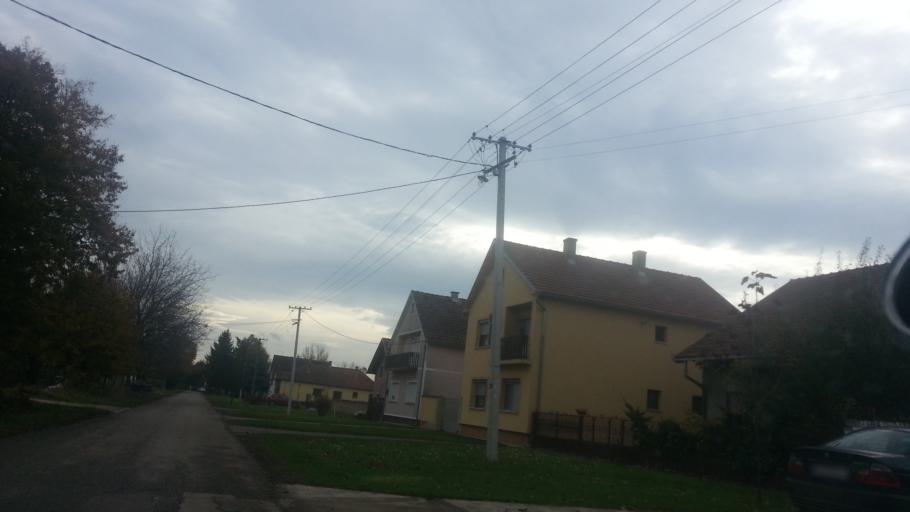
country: RS
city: Golubinci
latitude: 44.9920
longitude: 20.0579
